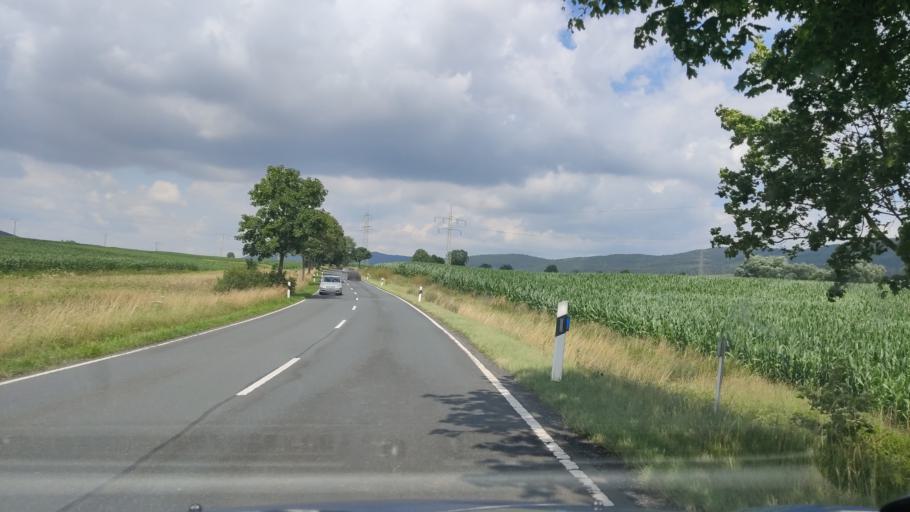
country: DE
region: Lower Saxony
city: Halle
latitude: 52.0083
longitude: 9.5578
